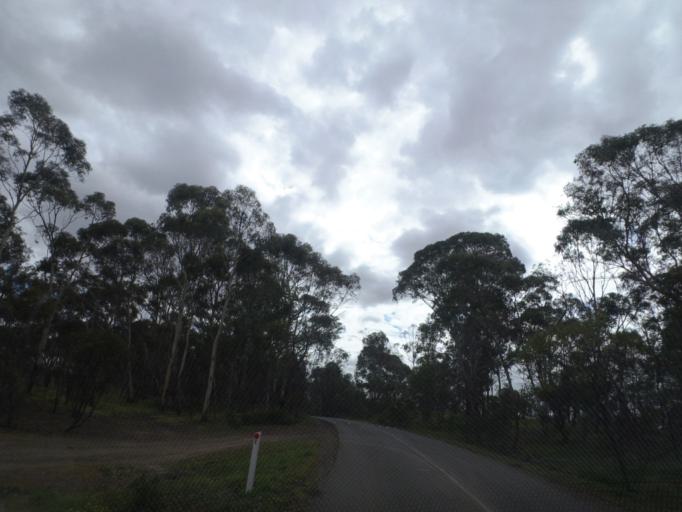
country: AU
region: Victoria
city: Plenty
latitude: -37.6700
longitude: 145.0943
